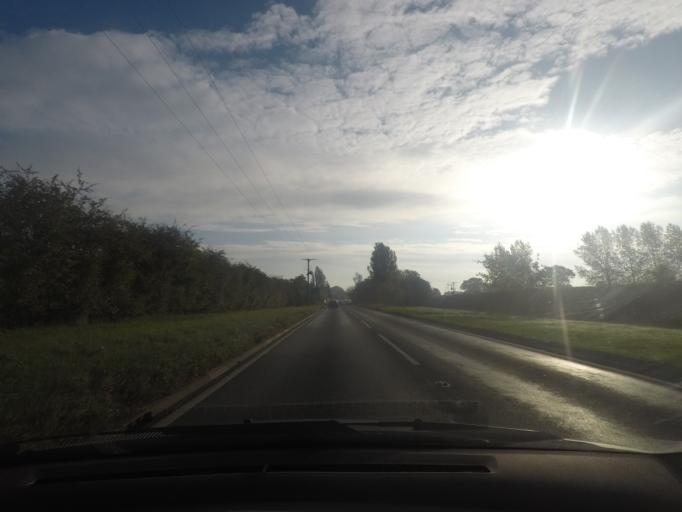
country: GB
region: England
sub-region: East Riding of Yorkshire
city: Wilberfoss
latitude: 53.9471
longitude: -0.8892
